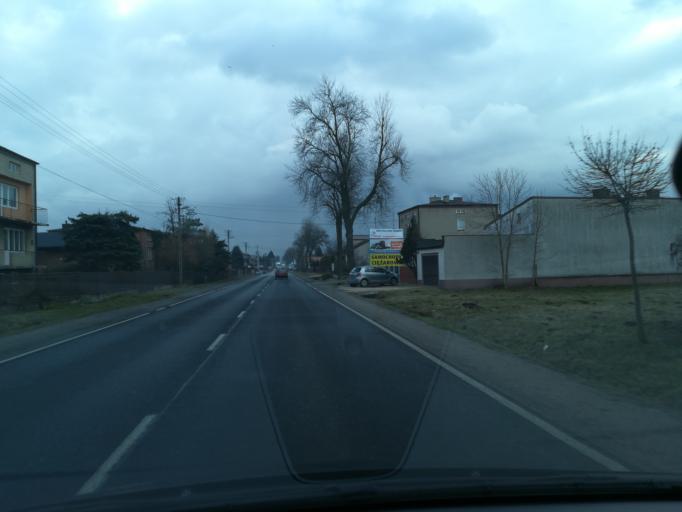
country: PL
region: Lodz Voivodeship
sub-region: Powiat radomszczanski
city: Radomsko
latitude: 51.0760
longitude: 19.4030
